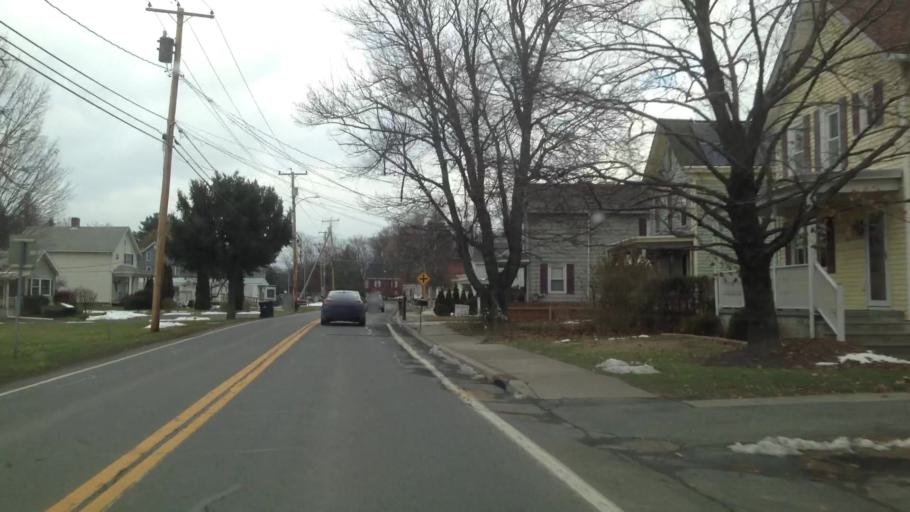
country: US
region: New York
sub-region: Ulster County
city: Glasco
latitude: 42.0419
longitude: -73.9525
